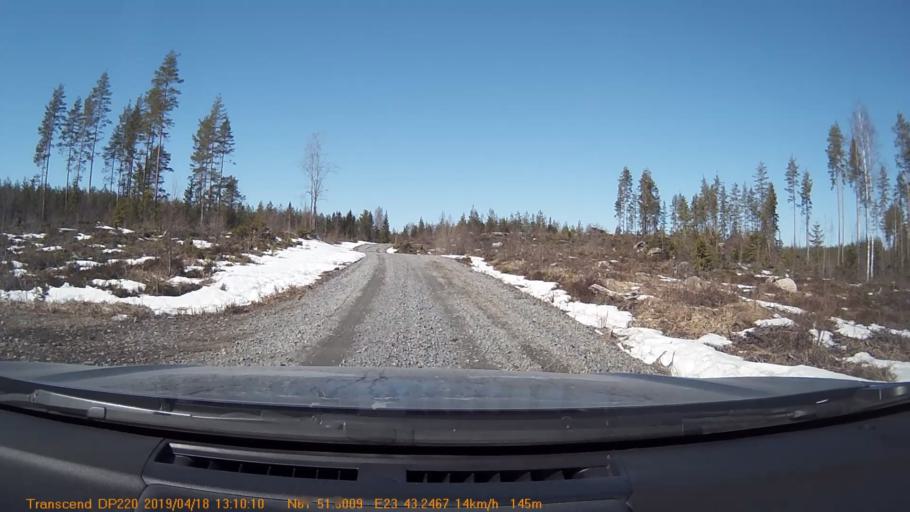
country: FI
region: Pirkanmaa
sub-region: Tampere
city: Kuru
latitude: 61.8584
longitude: 23.7208
